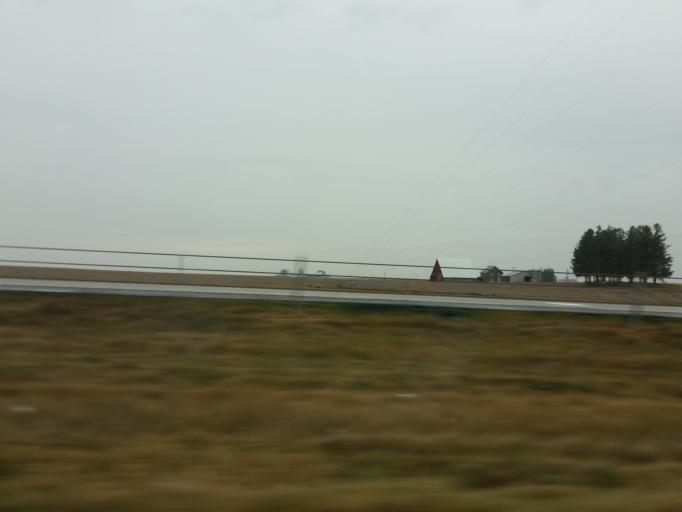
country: US
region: Iowa
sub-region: Muscatine County
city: Wilton
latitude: 41.6448
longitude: -91.1013
